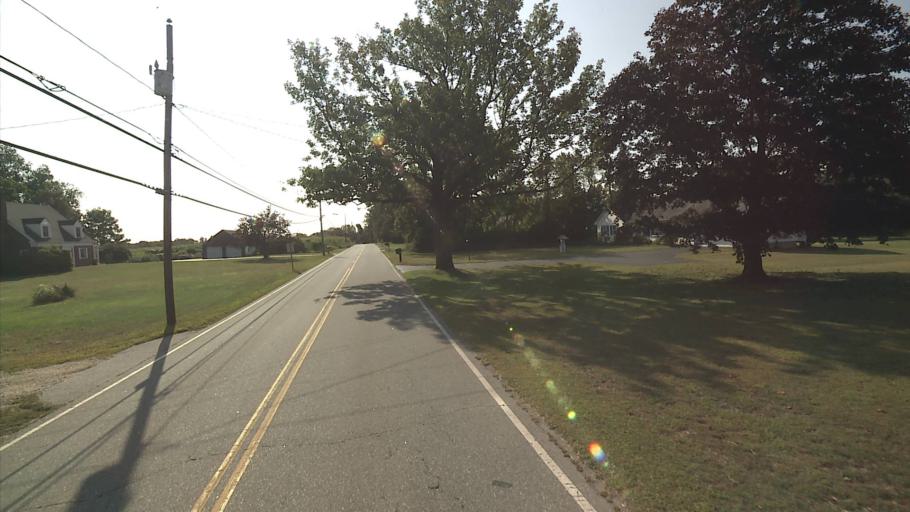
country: US
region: Connecticut
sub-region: Windham County
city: South Windham
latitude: 41.6095
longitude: -72.1768
